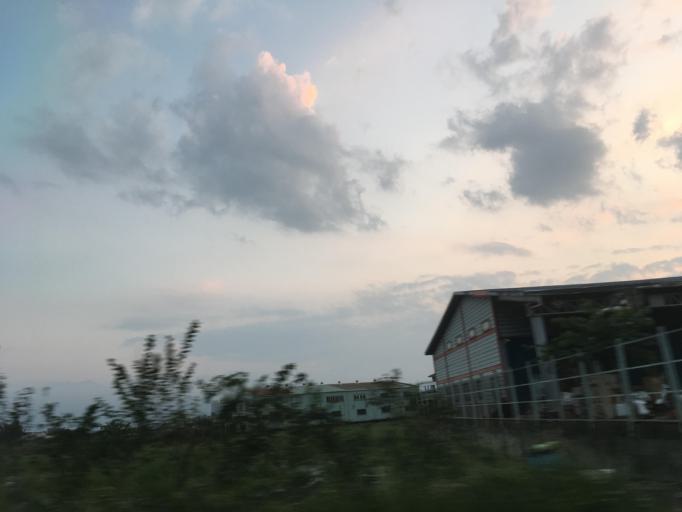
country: TW
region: Taiwan
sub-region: Yilan
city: Yilan
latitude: 24.6924
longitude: 121.7817
